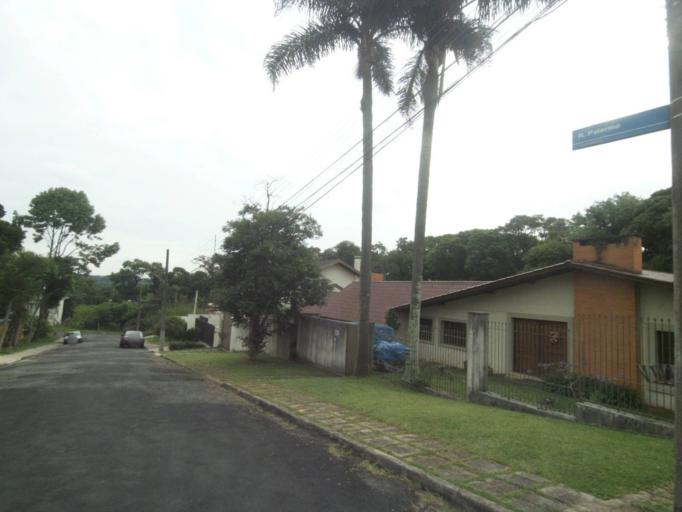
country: BR
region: Parana
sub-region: Curitiba
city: Curitiba
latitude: -25.4090
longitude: -49.3136
